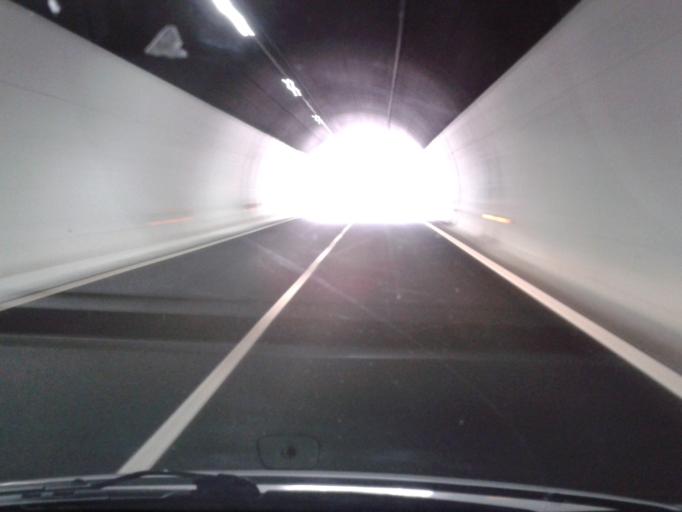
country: IT
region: Friuli Venezia Giulia
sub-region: Provincia di Udine
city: Chiusaforte
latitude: 46.4175
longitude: 13.3203
